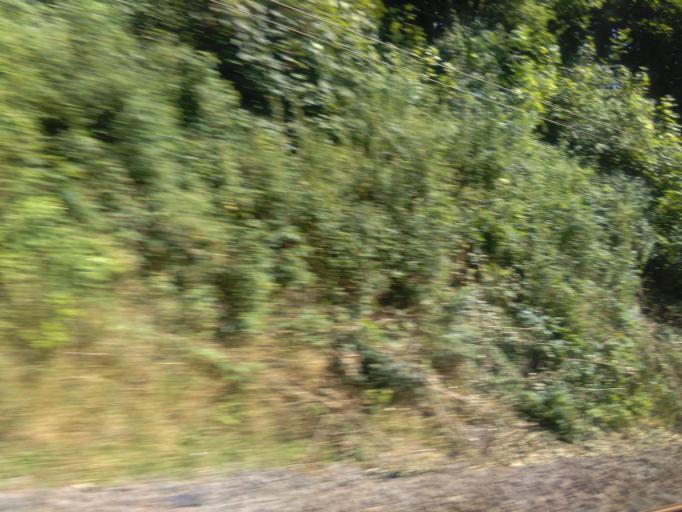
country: GB
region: England
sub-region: Hertfordshire
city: Harpenden
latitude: 51.8241
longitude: -0.3555
